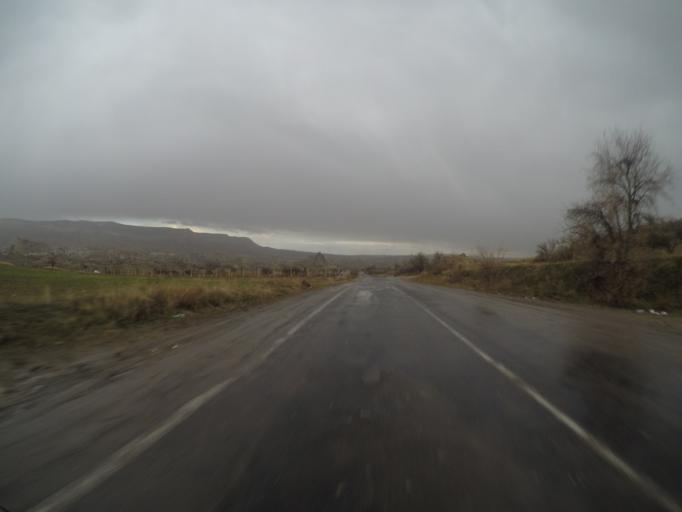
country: TR
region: Nevsehir
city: Goereme
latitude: 38.6633
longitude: 34.8301
